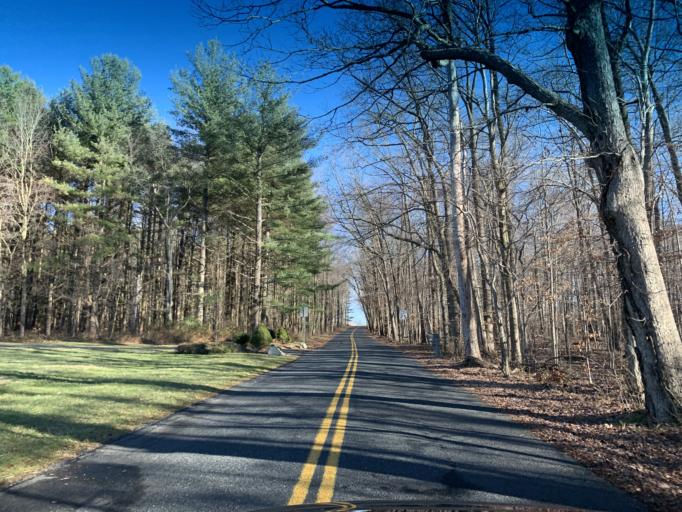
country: US
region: Maryland
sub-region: Harford County
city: Riverside
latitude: 39.5428
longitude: -76.2438
